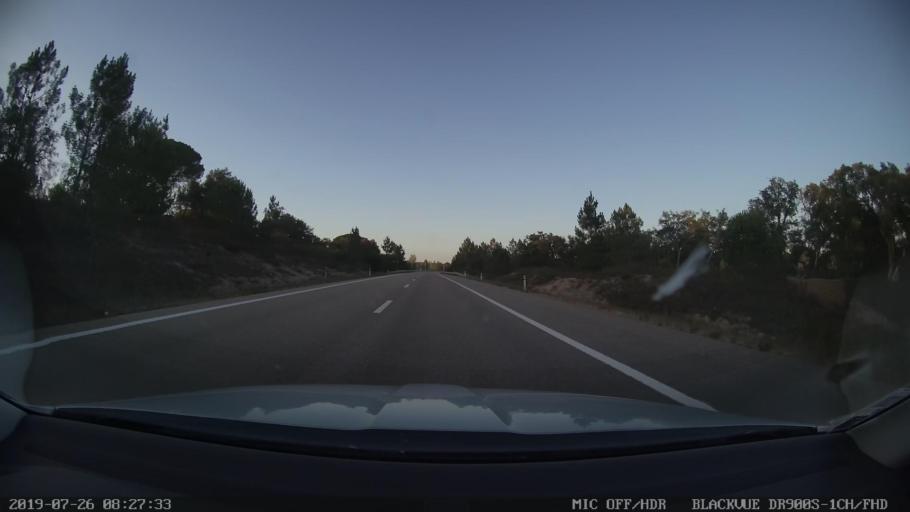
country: PT
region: Evora
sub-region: Vendas Novas
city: Vendas Novas
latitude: 38.6047
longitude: -8.6396
